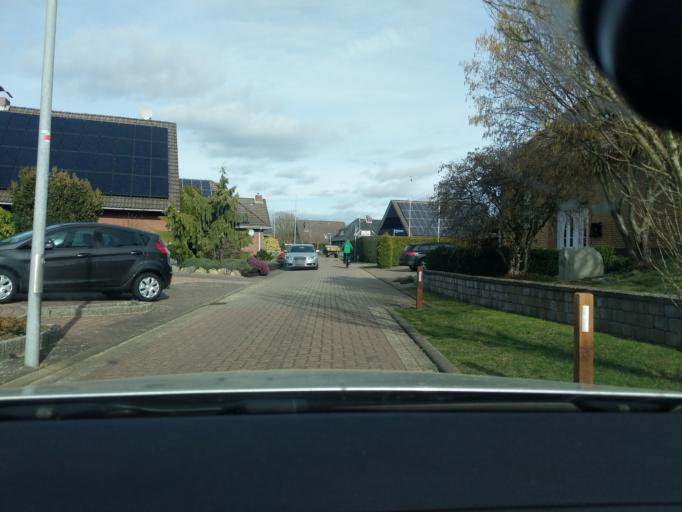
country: DE
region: Lower Saxony
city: Drochtersen
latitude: 53.6886
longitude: 9.4331
